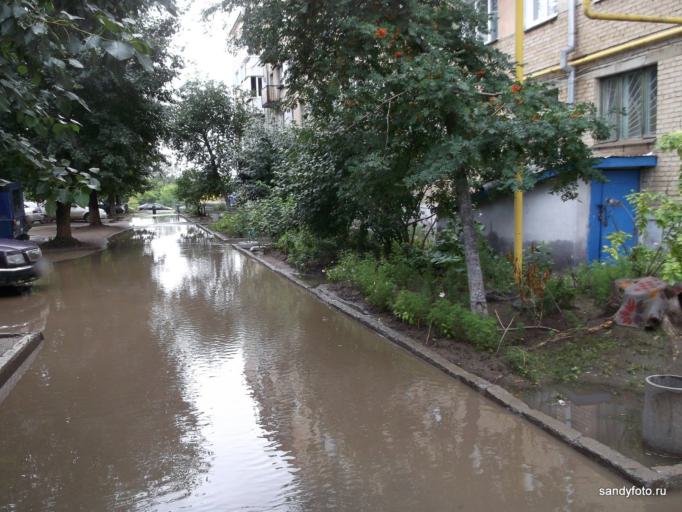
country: RU
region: Chelyabinsk
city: Troitsk
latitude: 54.0783
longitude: 61.5309
